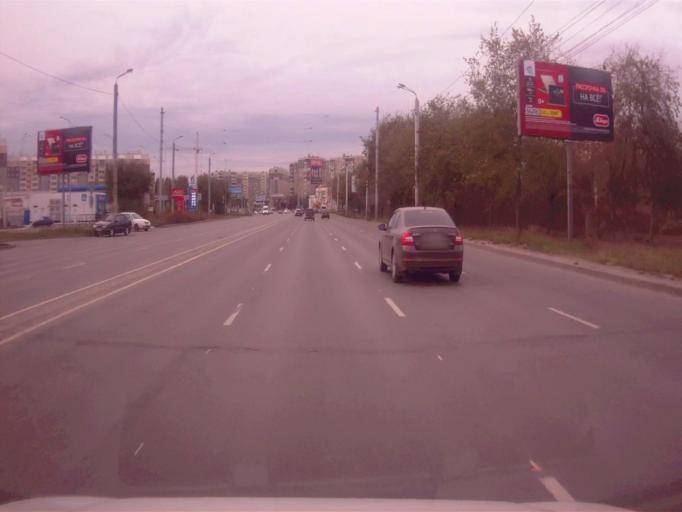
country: RU
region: Chelyabinsk
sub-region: Gorod Chelyabinsk
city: Chelyabinsk
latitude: 55.1768
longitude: 61.3763
